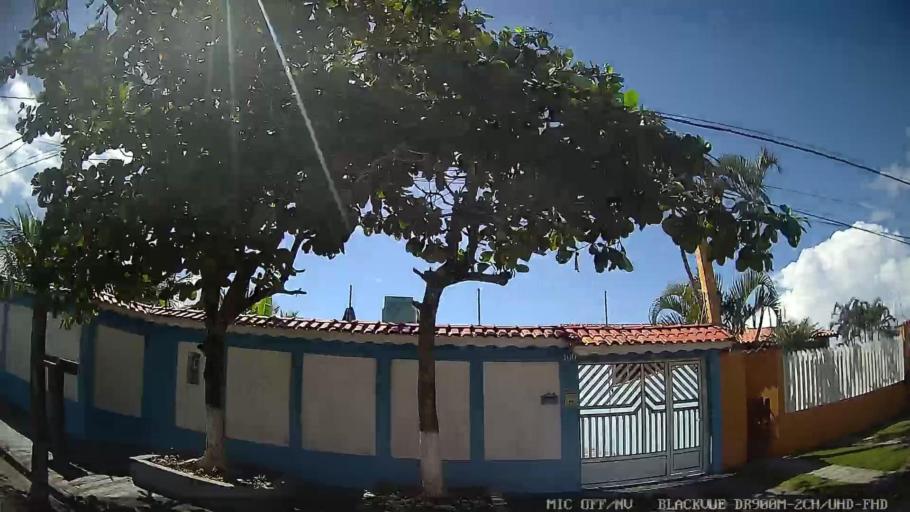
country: BR
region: Sao Paulo
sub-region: Itanhaem
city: Itanhaem
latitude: -24.2337
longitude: -46.8734
